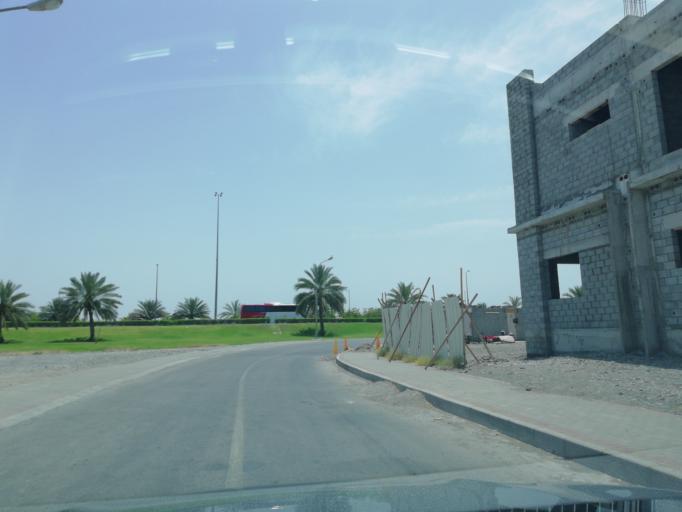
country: OM
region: Muhafazat Masqat
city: As Sib al Jadidah
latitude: 23.6578
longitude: 58.1973
